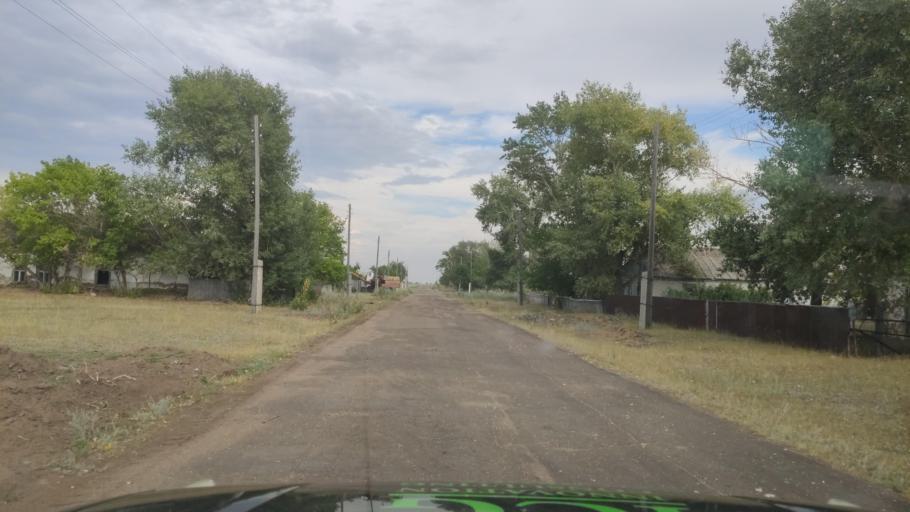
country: KZ
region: Pavlodar
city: Pavlodar
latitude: 52.5007
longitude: 77.5941
